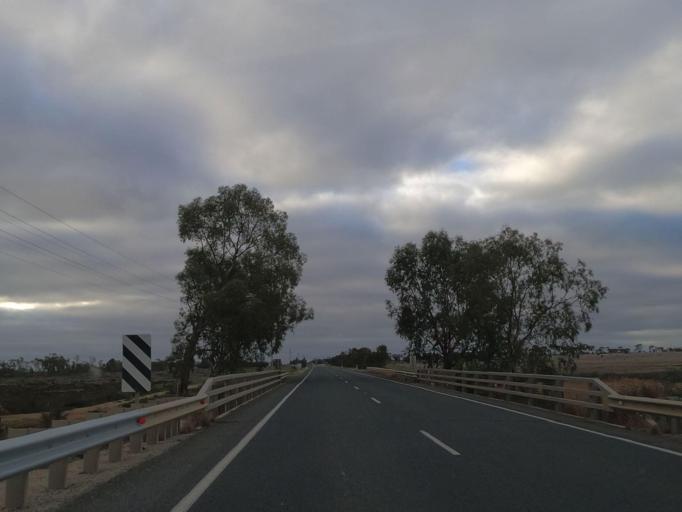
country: AU
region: Victoria
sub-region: Swan Hill
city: Swan Hill
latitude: -35.6192
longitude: 143.8034
